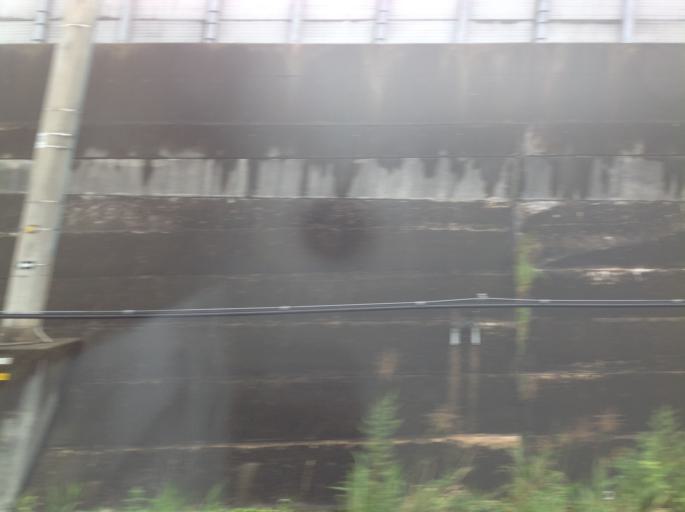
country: JP
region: Iwate
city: Ichinoseki
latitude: 38.9197
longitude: 141.1362
